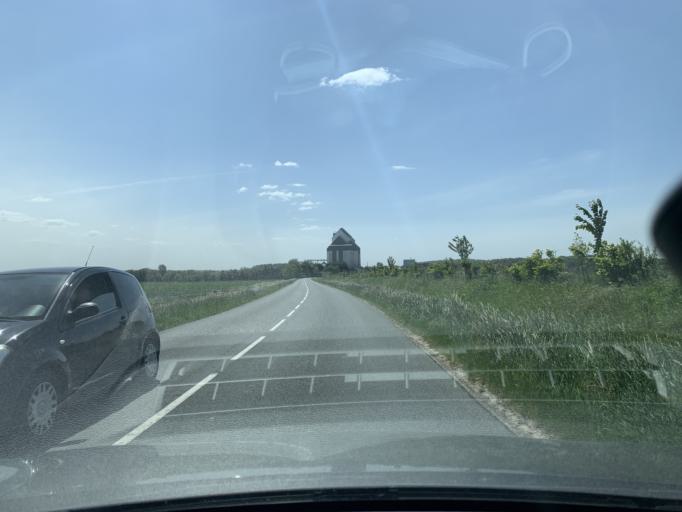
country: FR
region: Nord-Pas-de-Calais
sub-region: Departement du Nord
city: Proville
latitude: 50.1441
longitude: 3.1968
